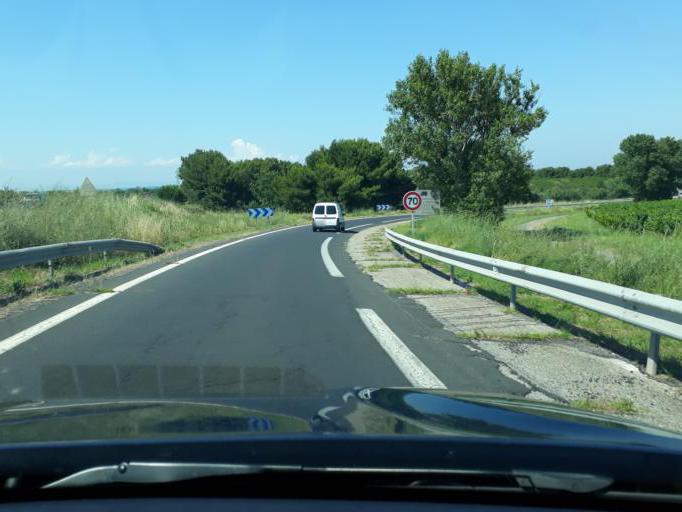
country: FR
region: Languedoc-Roussillon
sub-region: Departement de l'Herault
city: Le Cap d'Agde
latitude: 43.3063
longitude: 3.5081
